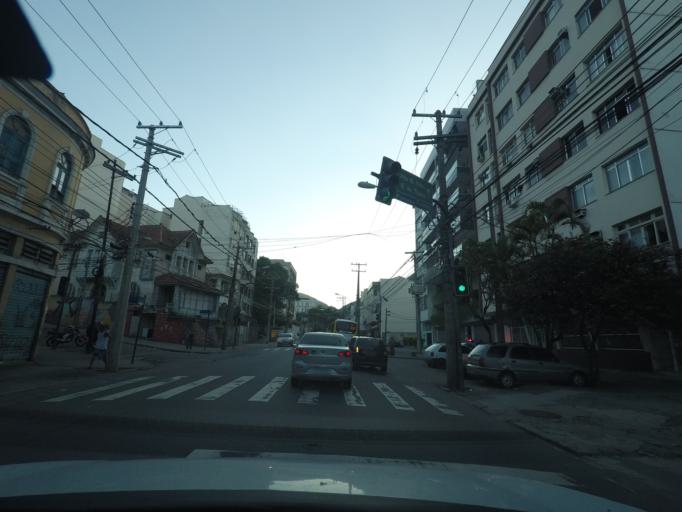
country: BR
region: Rio de Janeiro
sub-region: Rio De Janeiro
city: Rio de Janeiro
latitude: -22.9377
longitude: -43.2463
